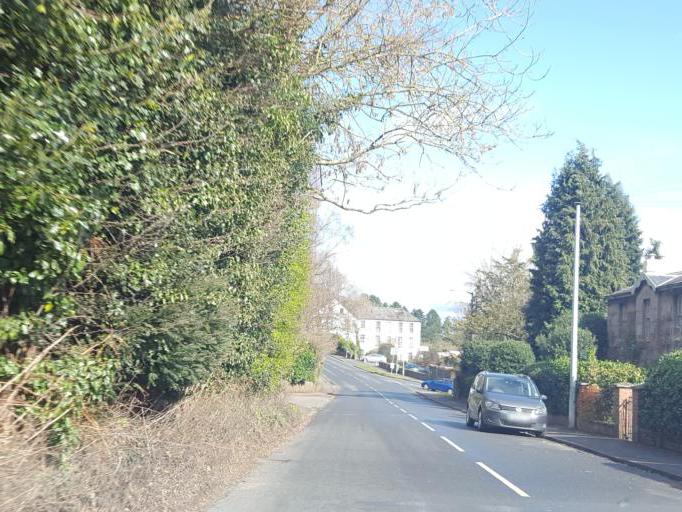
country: GB
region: England
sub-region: Worcestershire
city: Great Malvern
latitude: 52.0813
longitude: -2.3324
